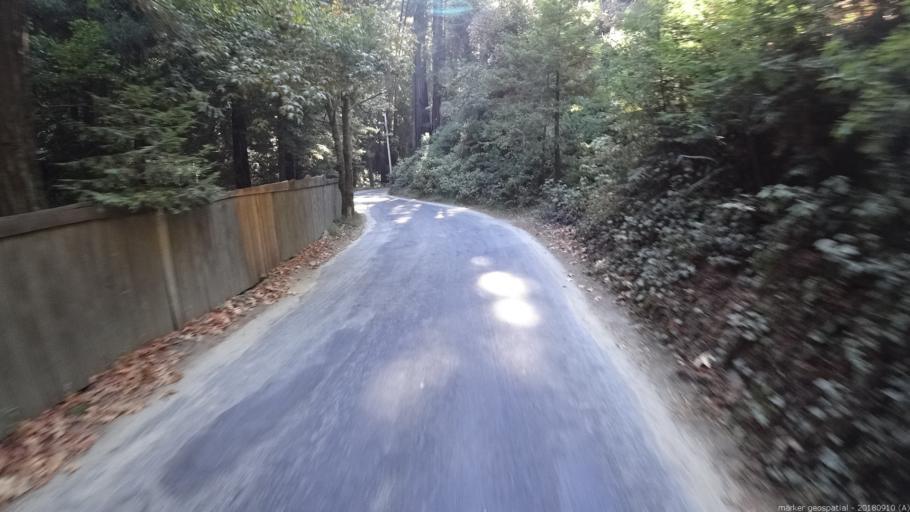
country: US
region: California
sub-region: Monterey County
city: Carmel Valley Village
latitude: 36.3968
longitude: -121.8818
